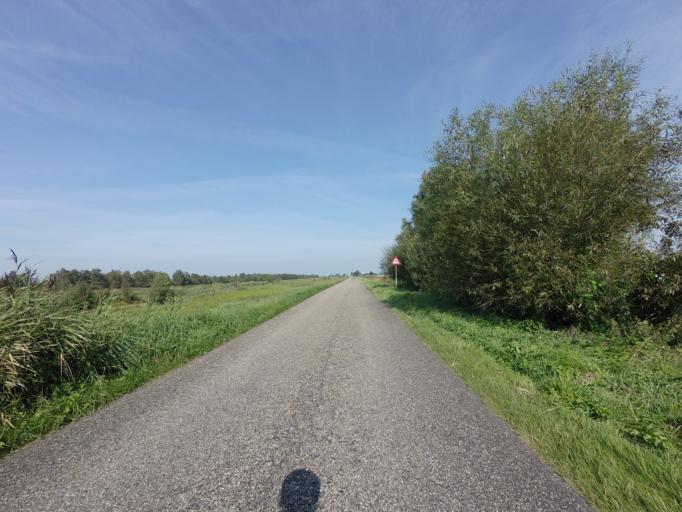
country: NL
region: Overijssel
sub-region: Gemeente Steenwijkerland
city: Oldemarkt
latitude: 52.8383
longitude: 5.9341
